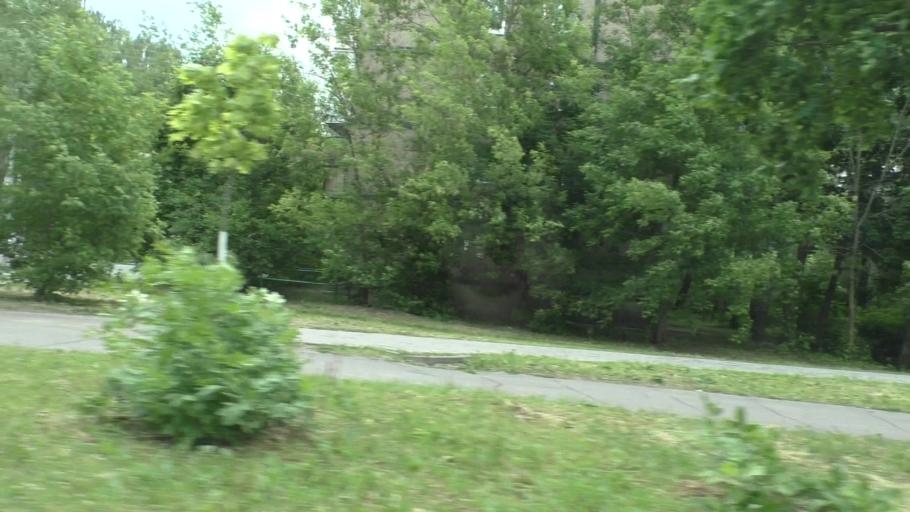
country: RU
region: Moskovskaya
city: Yegor'yevsk
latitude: 55.3702
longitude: 39.0527
